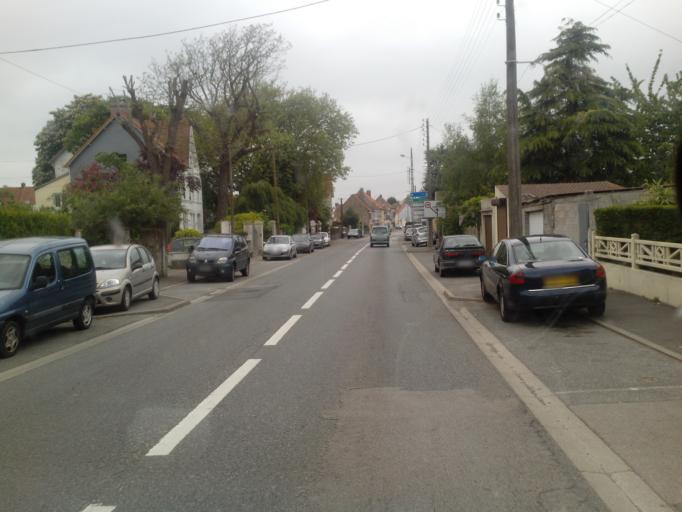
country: FR
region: Nord-Pas-de-Calais
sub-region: Departement du Pas-de-Calais
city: Saint-Etienne-au-Mont
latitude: 50.6764
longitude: 1.6354
